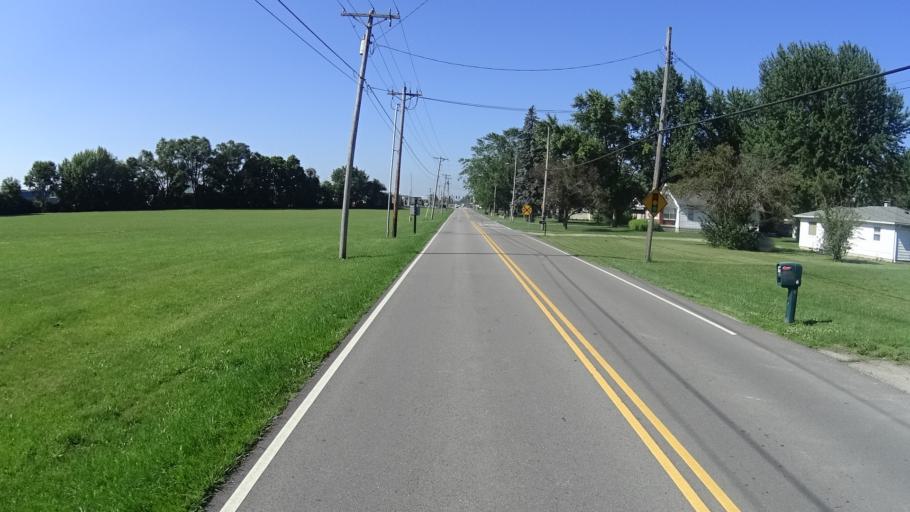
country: US
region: Indiana
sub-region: Madison County
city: Pendleton
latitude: 39.9859
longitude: -85.7511
